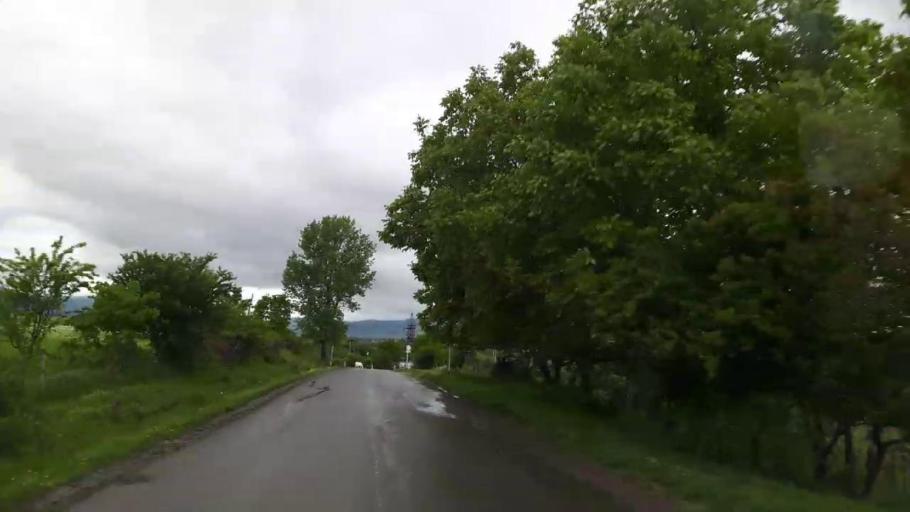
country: GE
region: Shida Kartli
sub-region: Khashuris Raioni
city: Khashuri
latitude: 41.9875
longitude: 43.6614
